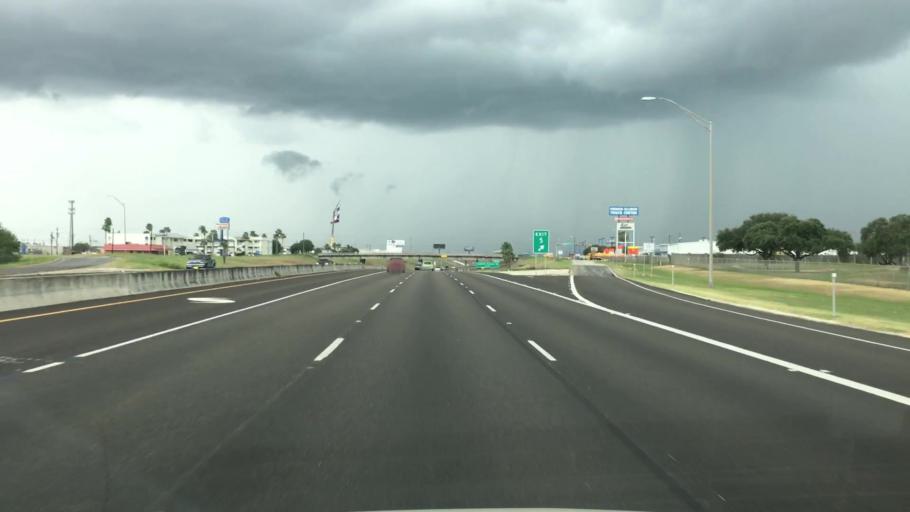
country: US
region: Texas
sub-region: Nueces County
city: Corpus Christi
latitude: 27.8049
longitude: -97.4812
